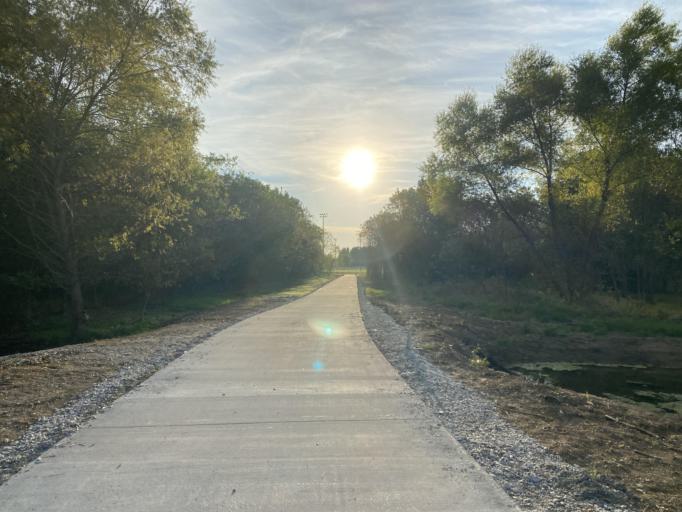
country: US
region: Arkansas
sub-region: Washington County
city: Johnson
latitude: 36.1034
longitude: -94.2032
